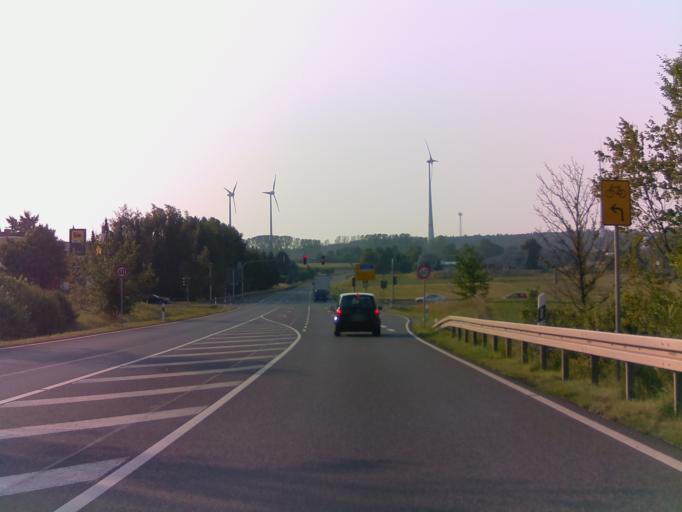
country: DE
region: Hesse
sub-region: Regierungsbezirk Kassel
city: Friedewald
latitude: 50.8840
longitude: 9.8677
